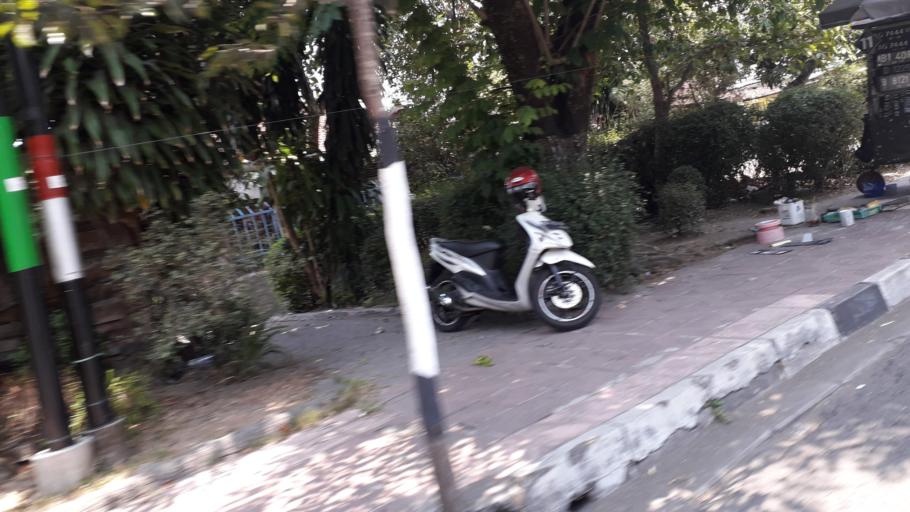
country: ID
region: Daerah Istimewa Yogyakarta
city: Yogyakarta
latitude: -7.7861
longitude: 110.3603
